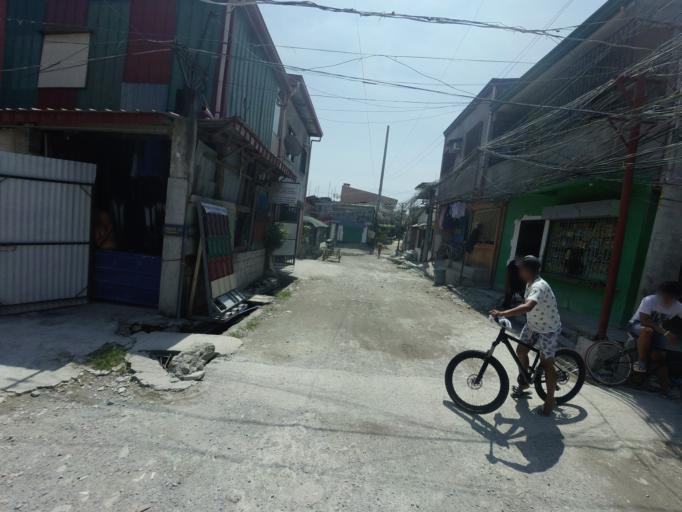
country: PH
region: Calabarzon
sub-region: Province of Rizal
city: Taytay
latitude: 14.5394
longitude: 121.1078
